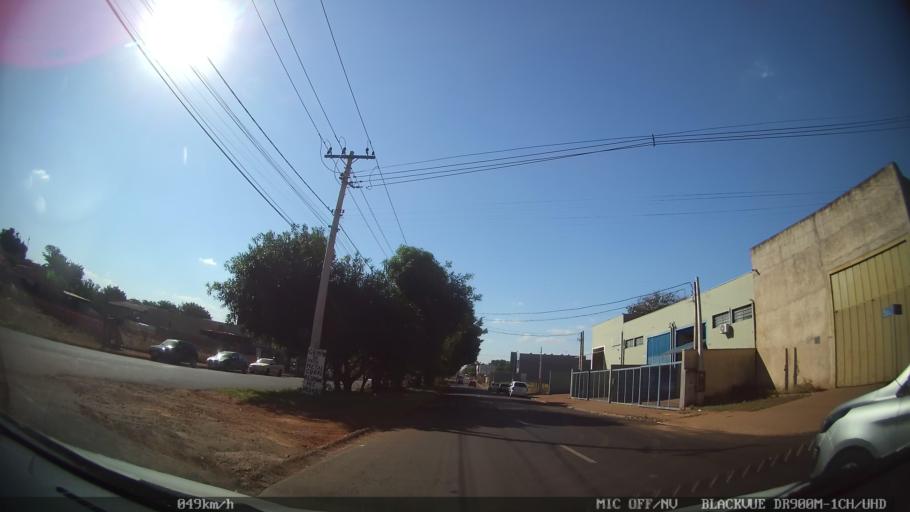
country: BR
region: Sao Paulo
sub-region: Ribeirao Preto
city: Ribeirao Preto
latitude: -21.1578
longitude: -47.7696
